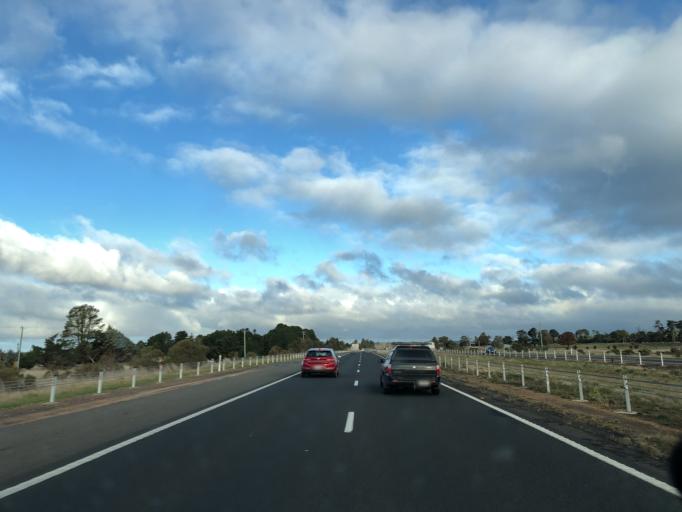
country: AU
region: Victoria
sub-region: Mount Alexander
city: Castlemaine
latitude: -37.2050
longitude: 144.4091
